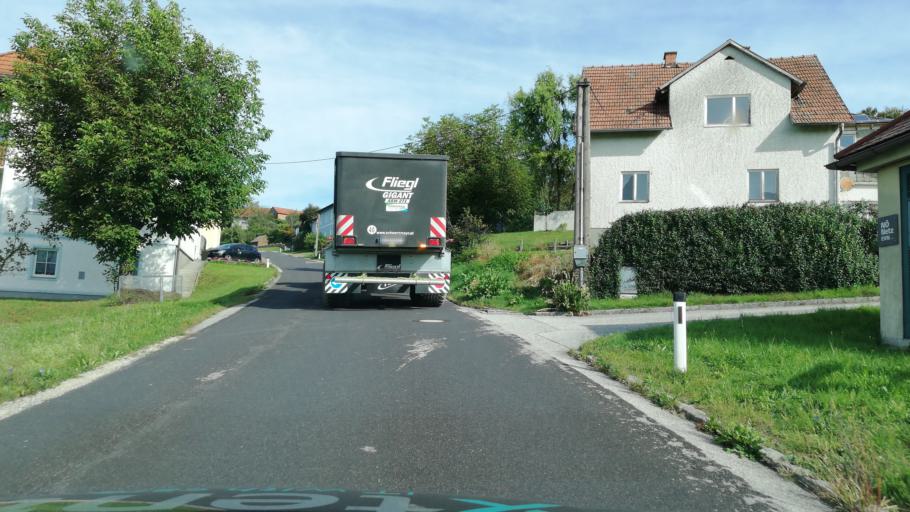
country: AT
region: Lower Austria
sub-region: Politischer Bezirk Amstetten
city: Behamberg
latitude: 48.0420
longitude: 14.4706
